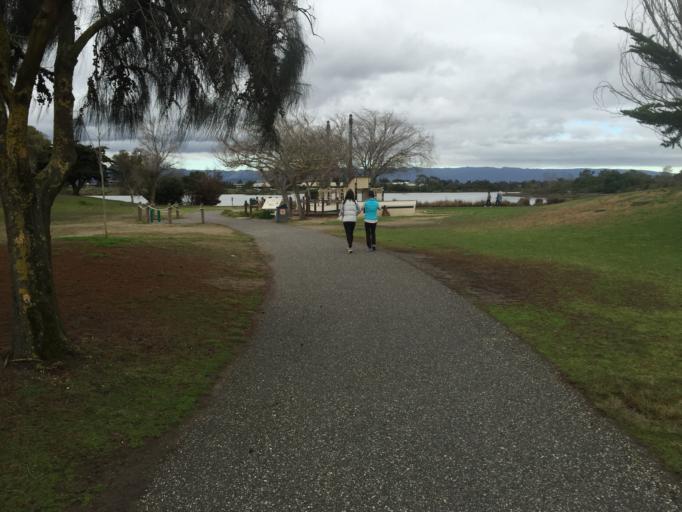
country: US
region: California
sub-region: Santa Clara County
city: Mountain View
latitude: 37.4343
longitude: -122.0895
